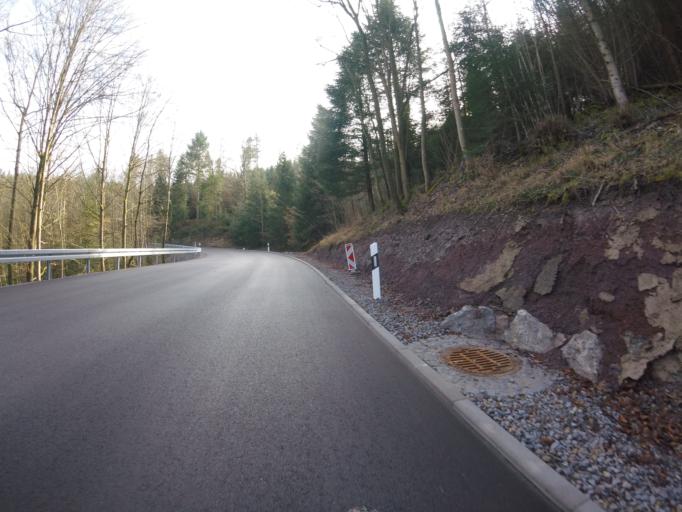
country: DE
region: Baden-Wuerttemberg
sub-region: Regierungsbezirk Stuttgart
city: Murrhardt
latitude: 48.9858
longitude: 9.5999
